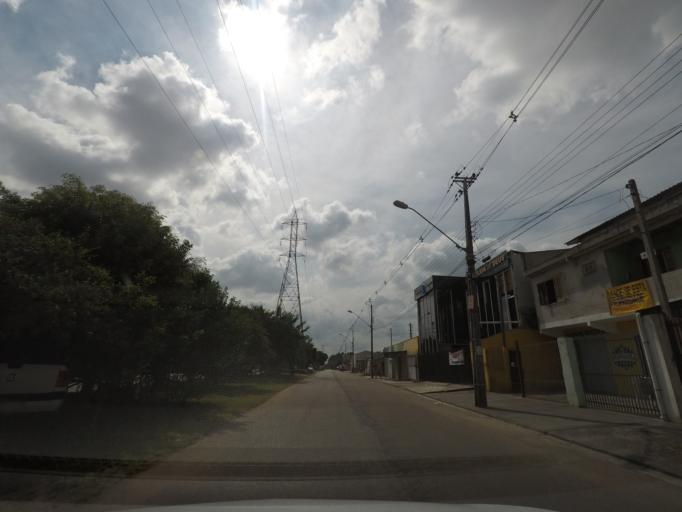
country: BR
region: Parana
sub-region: Pinhais
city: Pinhais
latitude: -25.4574
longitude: -49.1972
